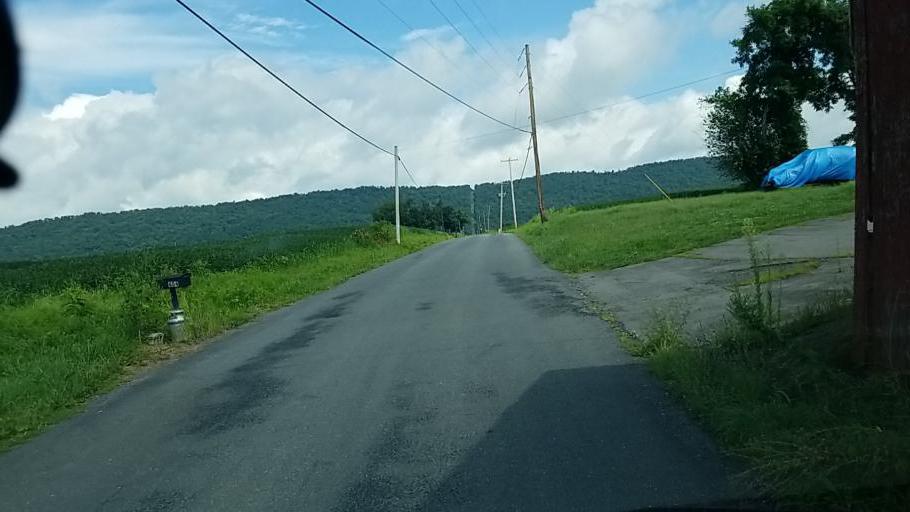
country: US
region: Pennsylvania
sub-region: Dauphin County
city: Millersburg
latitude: 40.5671
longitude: -76.9290
